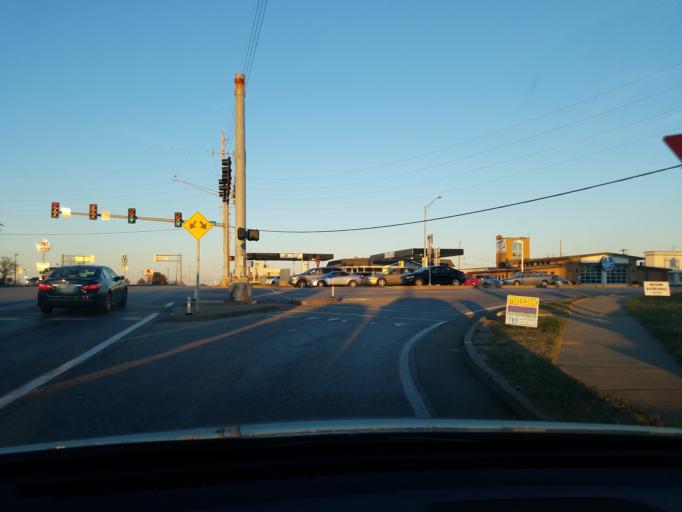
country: US
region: Missouri
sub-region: Saint Louis County
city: Mehlville
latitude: 38.5056
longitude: -90.3261
